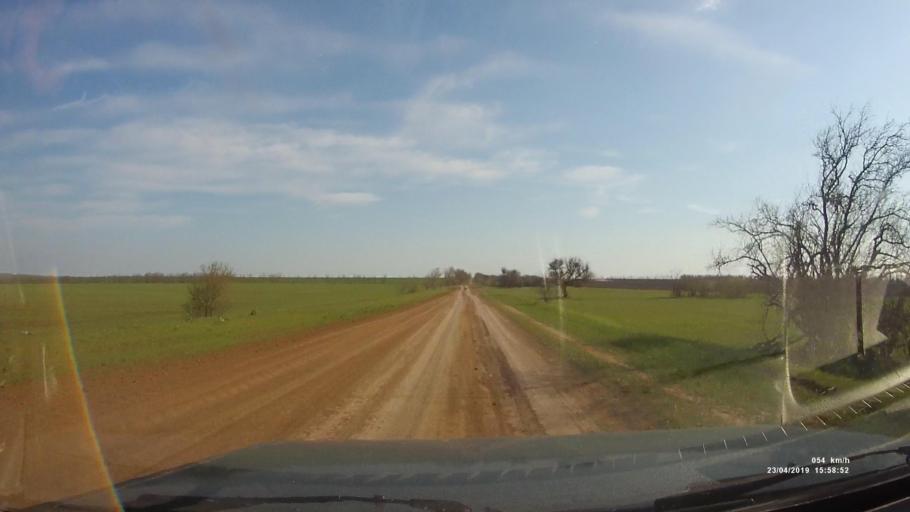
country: RU
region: Rostov
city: Remontnoye
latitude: 46.5207
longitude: 43.1095
